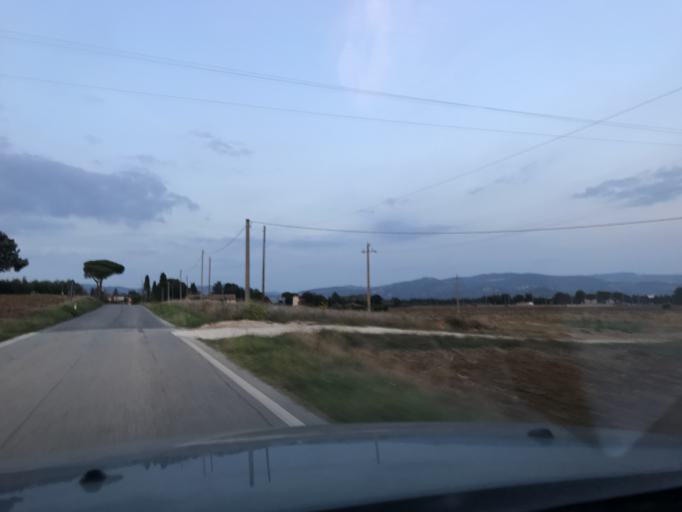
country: IT
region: Umbria
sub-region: Provincia di Perugia
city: Via Lippia
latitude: 43.0919
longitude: 12.4884
